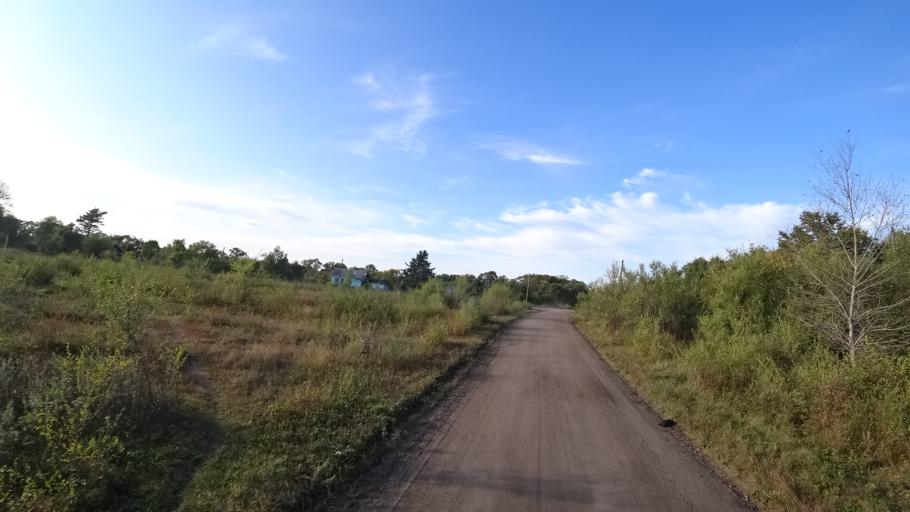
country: RU
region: Amur
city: Arkhara
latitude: 49.3537
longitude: 130.1100
